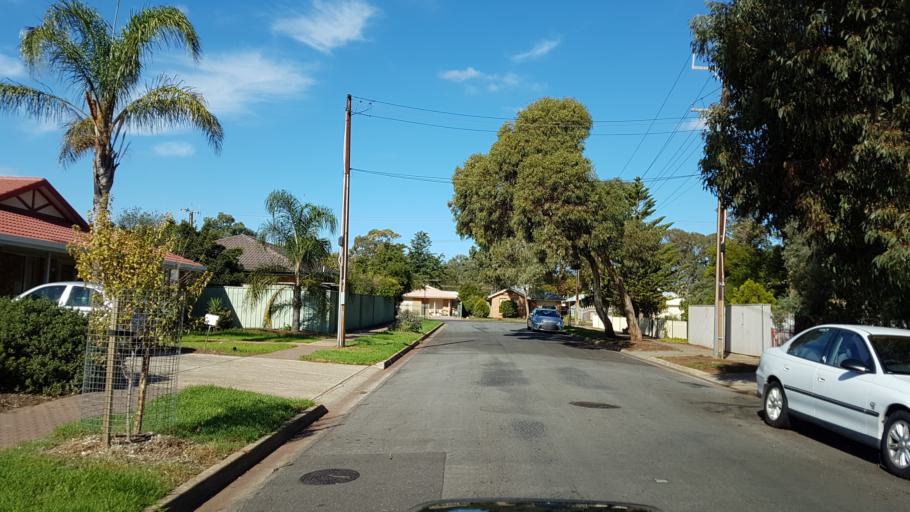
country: AU
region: South Australia
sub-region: Salisbury
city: Salisbury
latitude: -34.7533
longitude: 138.6393
